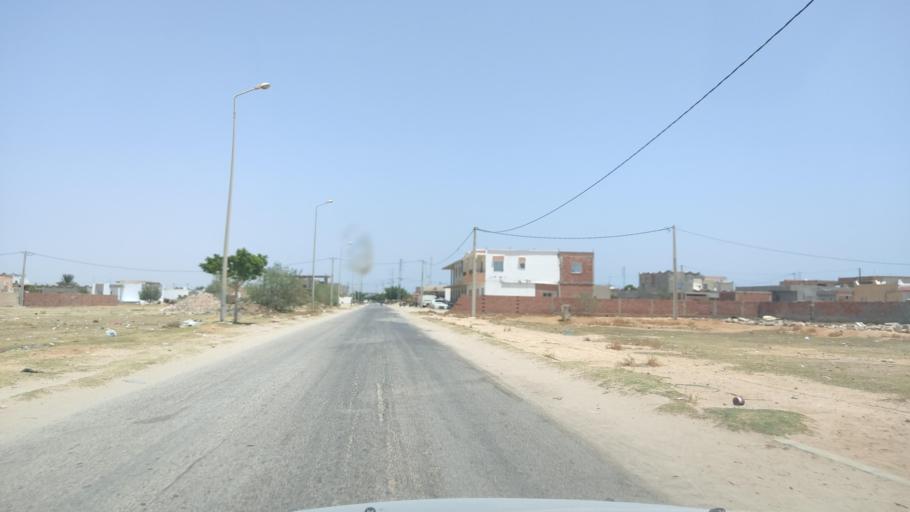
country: TN
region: Safaqis
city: Sfax
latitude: 34.6642
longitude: 10.7069
